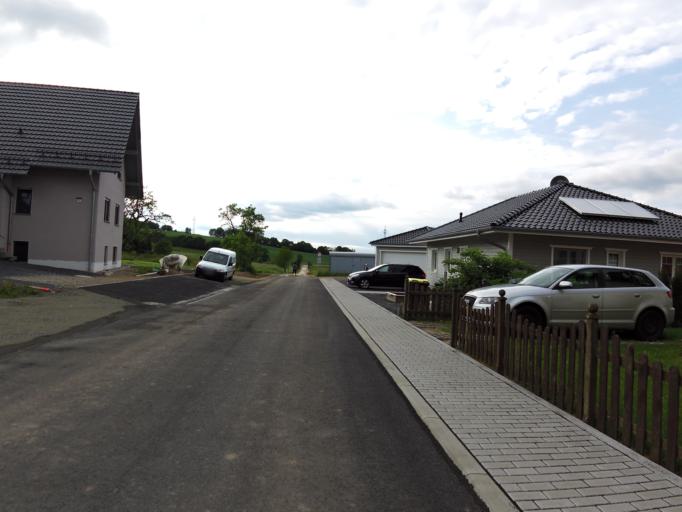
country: DE
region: Thuringia
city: Frauensee
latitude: 50.9081
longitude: 10.0976
